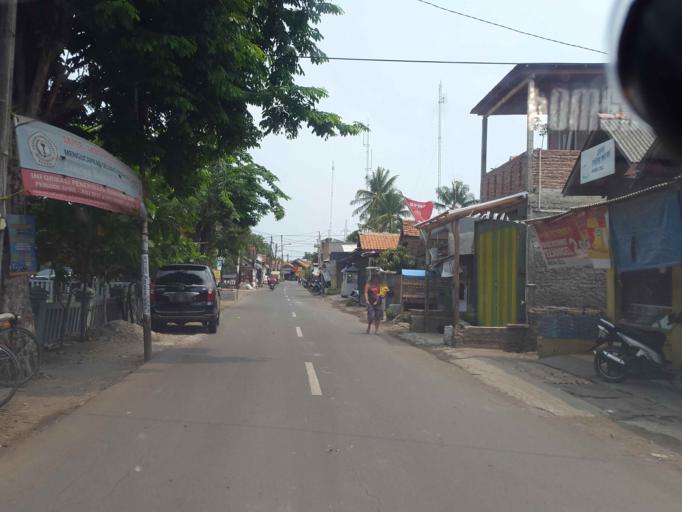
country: ID
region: West Java
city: Rengasdengklok
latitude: -6.2694
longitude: 107.2682
